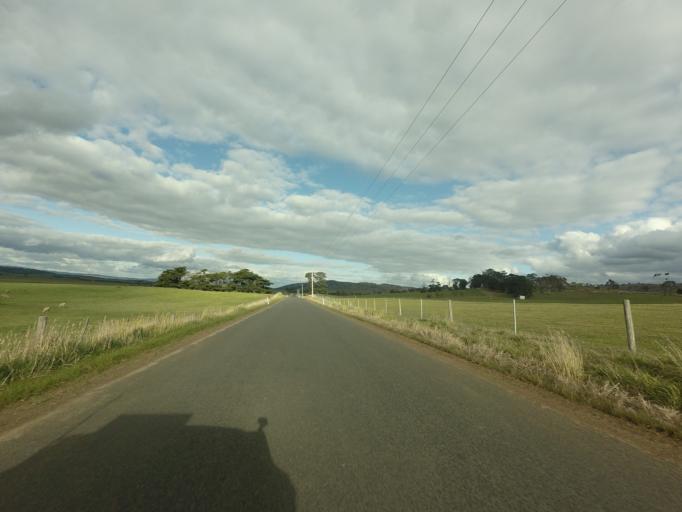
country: AU
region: Tasmania
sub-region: Northern Midlands
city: Evandale
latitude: -41.8946
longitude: 147.3390
